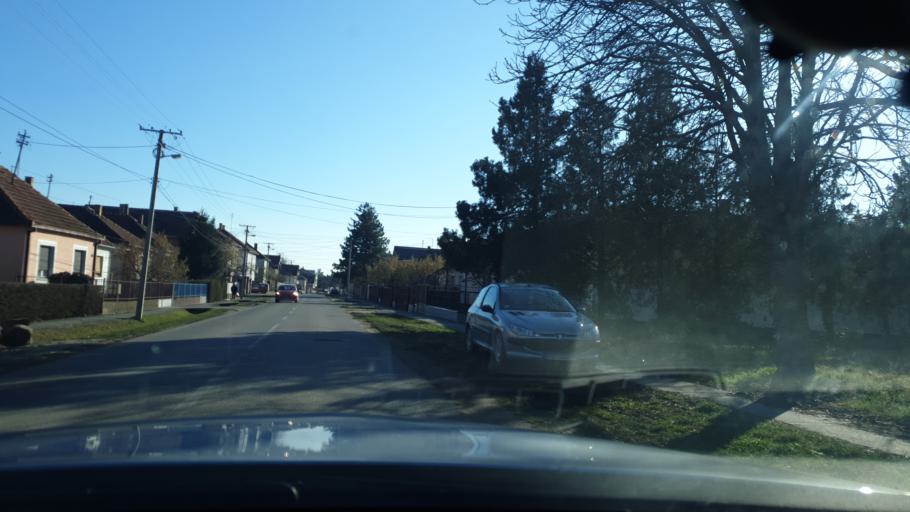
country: RS
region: Autonomna Pokrajina Vojvodina
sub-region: Sremski Okrug
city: Ruma
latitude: 45.0163
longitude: 19.8167
